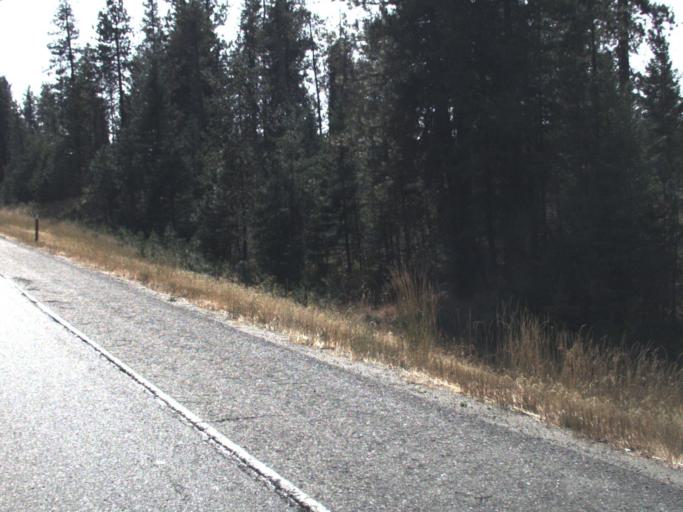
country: US
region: Washington
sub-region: Stevens County
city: Chewelah
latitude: 48.0993
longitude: -117.6390
